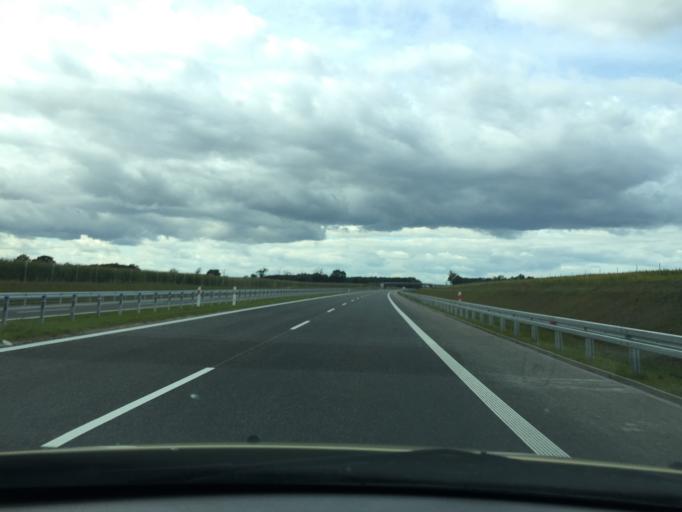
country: PL
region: Greater Poland Voivodeship
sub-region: Powiat jarocinski
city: Jarocin
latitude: 51.9853
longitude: 17.5136
